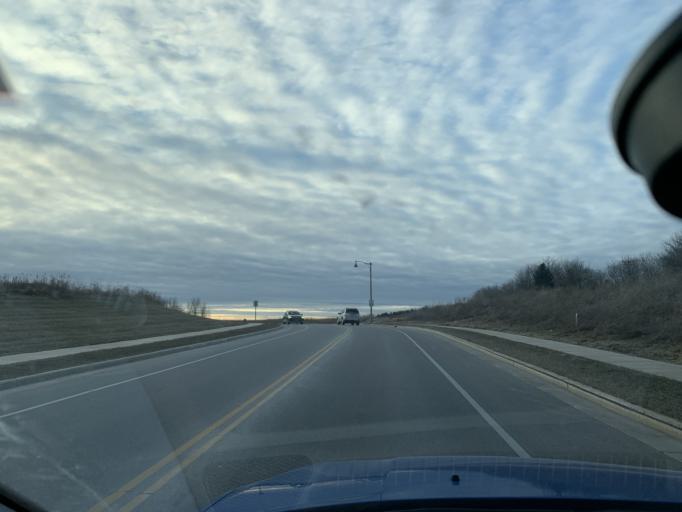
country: US
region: Wisconsin
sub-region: Dane County
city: Fitchburg
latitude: 43.0186
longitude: -89.4792
